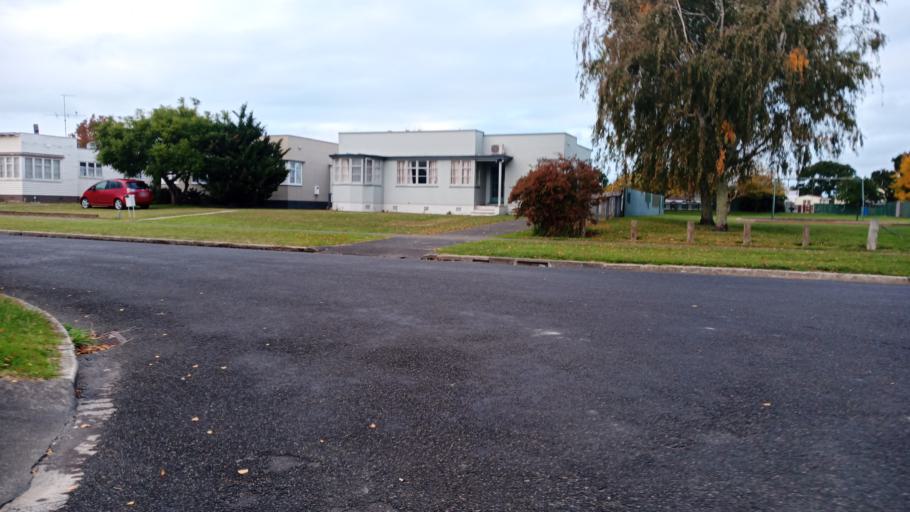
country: NZ
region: Gisborne
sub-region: Gisborne District
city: Gisborne
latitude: -38.6598
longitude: 178.0036
